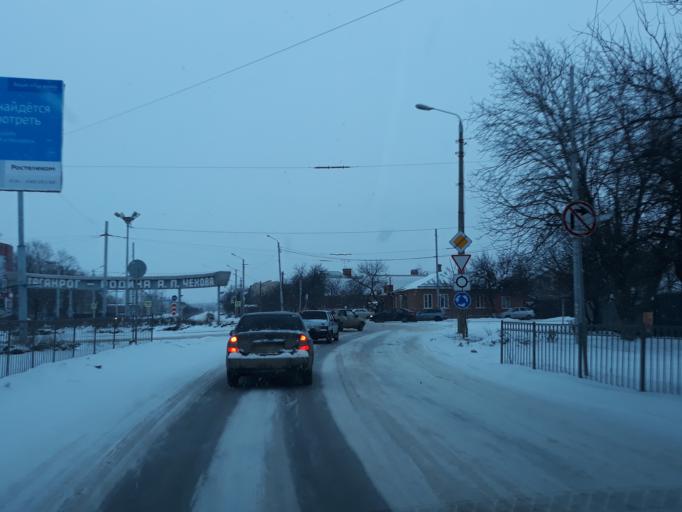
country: RU
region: Rostov
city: Taganrog
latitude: 47.2710
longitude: 38.9206
